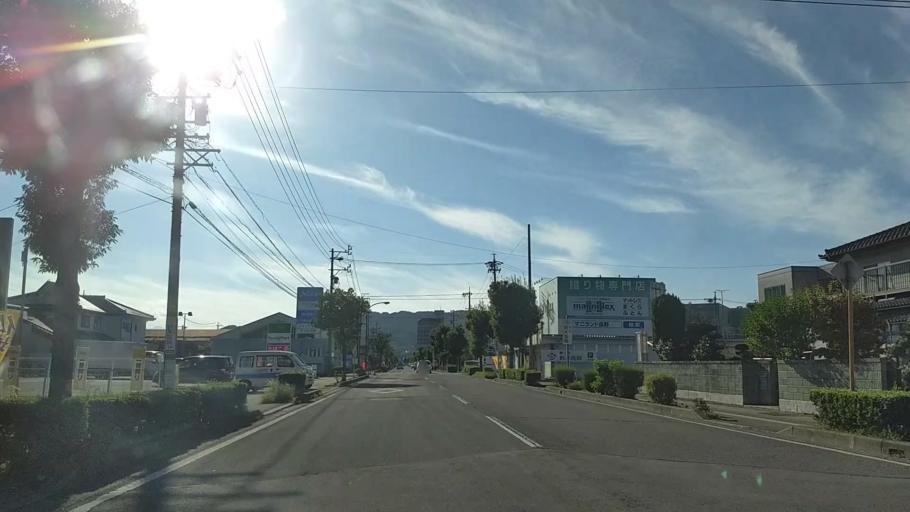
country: JP
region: Nagano
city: Nagano-shi
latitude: 36.5817
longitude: 138.1553
